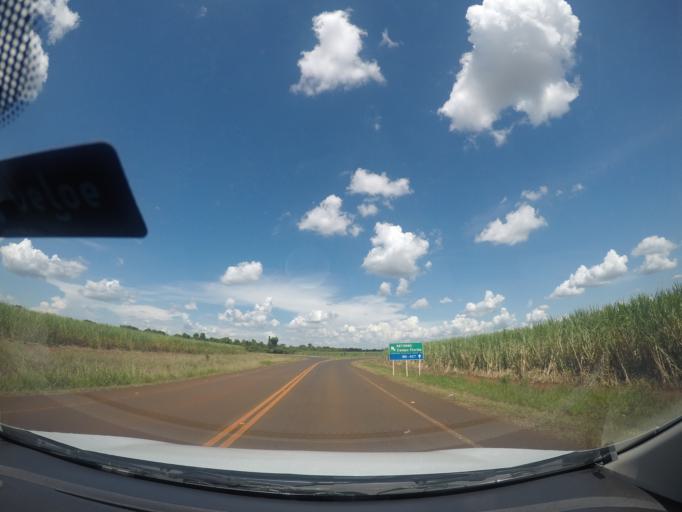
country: BR
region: Minas Gerais
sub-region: Conceicao Das Alagoas
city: Conceicao das Alagoas
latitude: -19.9285
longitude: -48.6627
